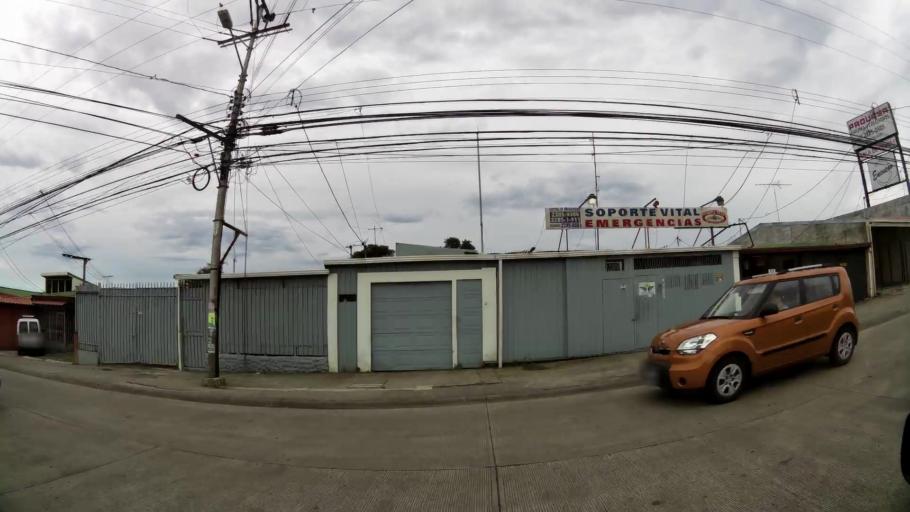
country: CR
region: San Jose
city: Purral
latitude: 9.9648
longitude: -84.0306
